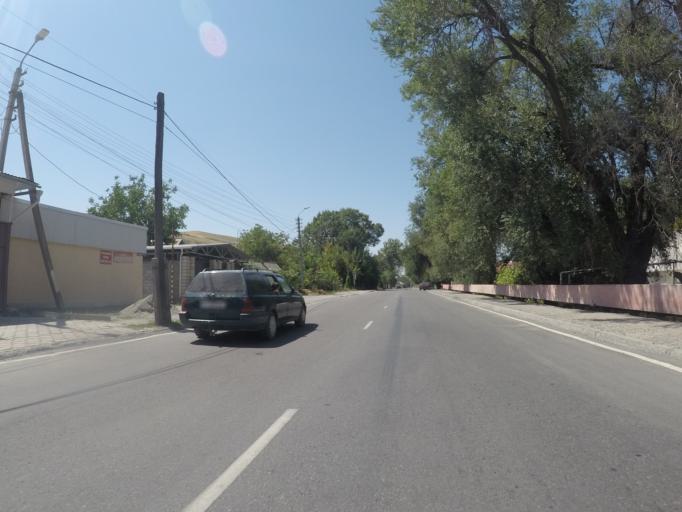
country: KG
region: Chuy
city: Bishkek
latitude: 42.8043
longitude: 74.5744
